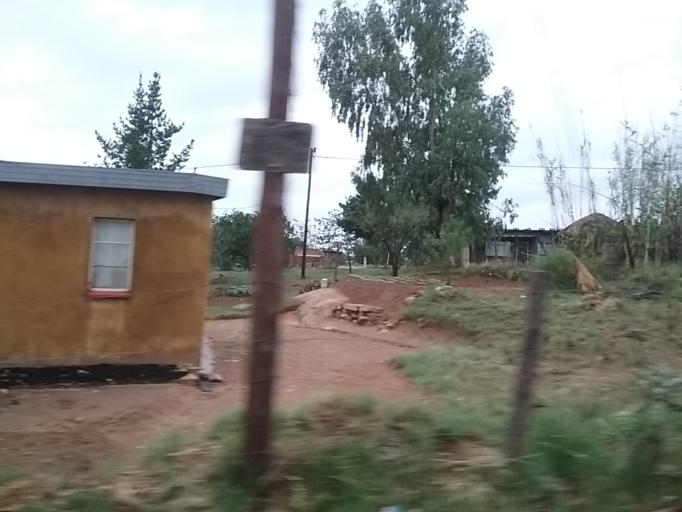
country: LS
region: Berea
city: Teyateyaneng
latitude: -29.1356
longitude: 27.7343
